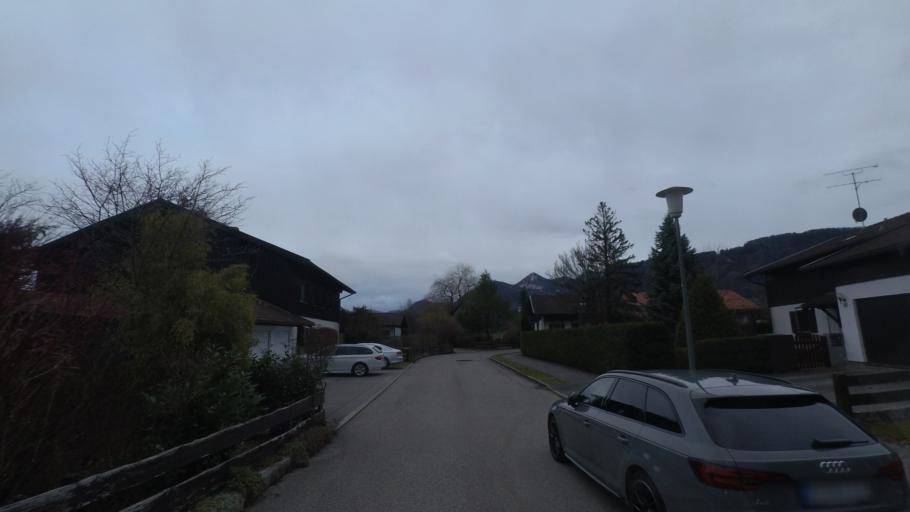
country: DE
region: Bavaria
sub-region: Upper Bavaria
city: Bernau am Chiemsee
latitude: 47.8132
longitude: 12.3829
